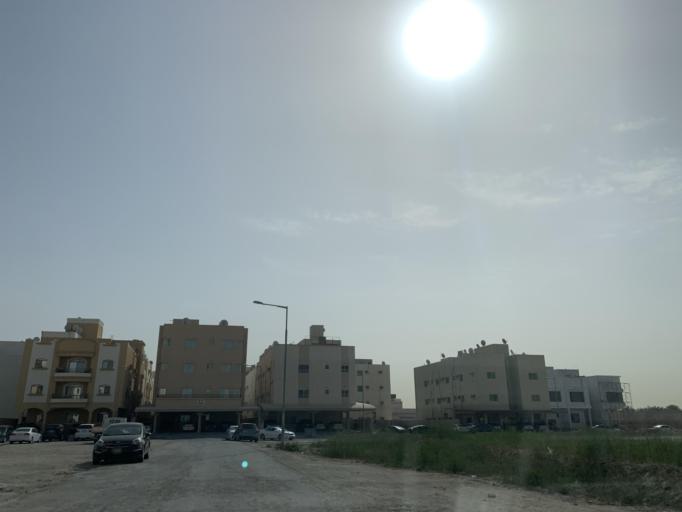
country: BH
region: Northern
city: Madinat `Isa
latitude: 26.1783
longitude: 50.5649
